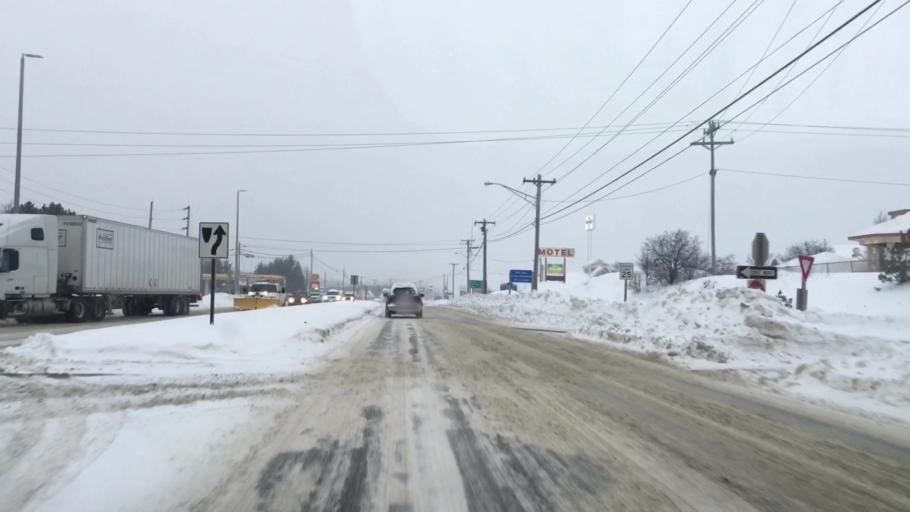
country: US
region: Maine
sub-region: Aroostook County
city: Houlton
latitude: 46.1404
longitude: -67.8400
